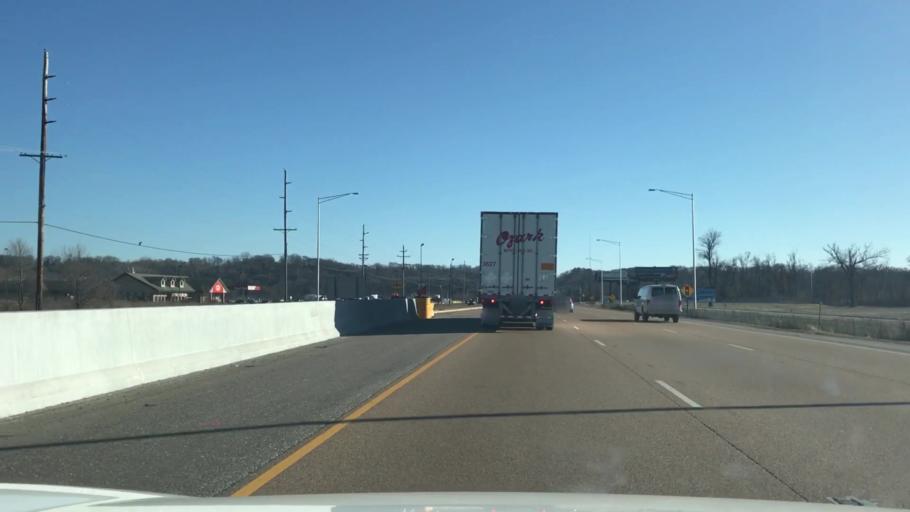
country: US
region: Illinois
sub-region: Saint Clair County
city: Alorton
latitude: 38.5767
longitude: -90.1016
